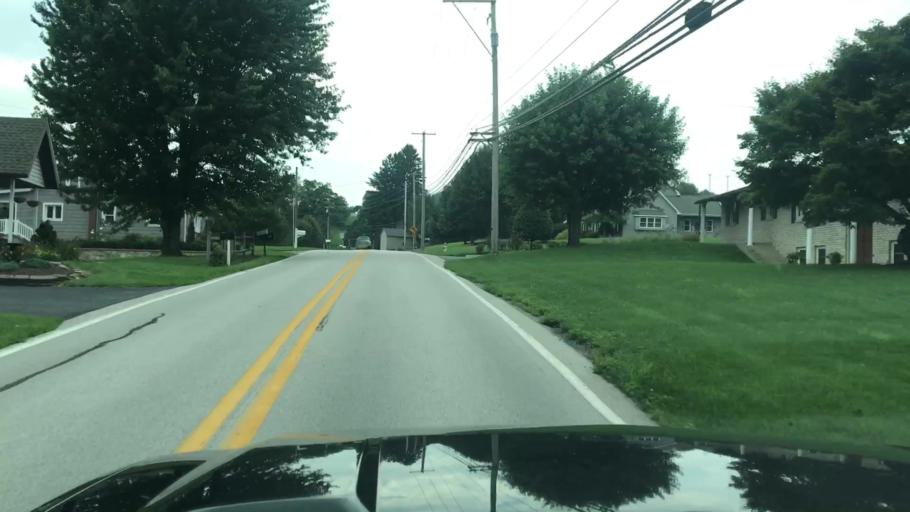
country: US
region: Pennsylvania
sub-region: Dauphin County
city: Steelton
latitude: 40.1827
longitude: -76.8592
